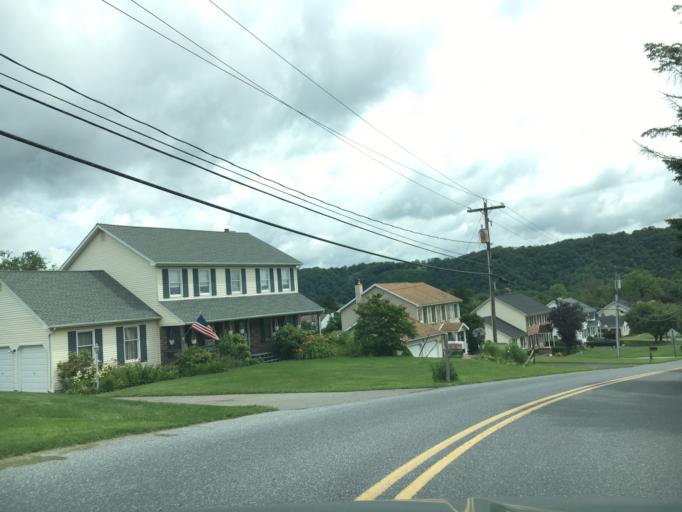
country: US
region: Pennsylvania
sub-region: Lehigh County
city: Laurys Station
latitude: 40.7232
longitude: -75.5356
